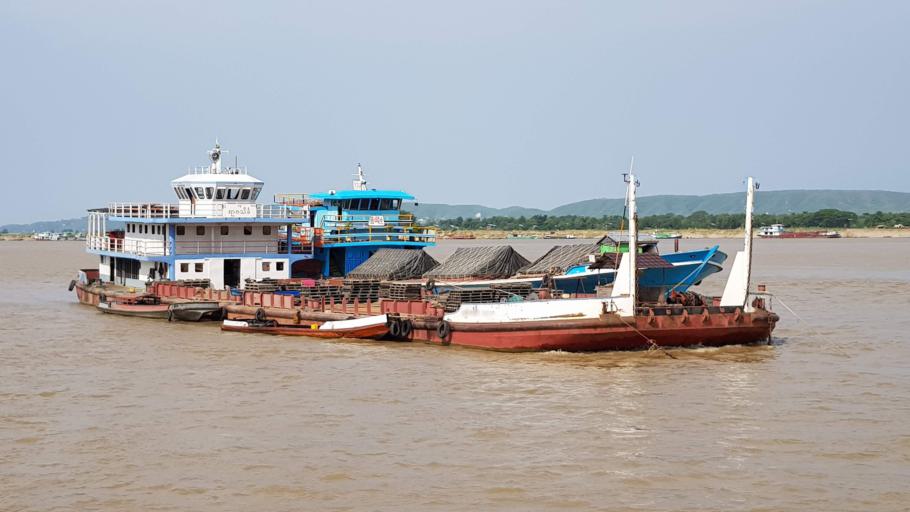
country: MM
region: Mandalay
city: Mandalay
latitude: 21.9847
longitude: 96.0583
